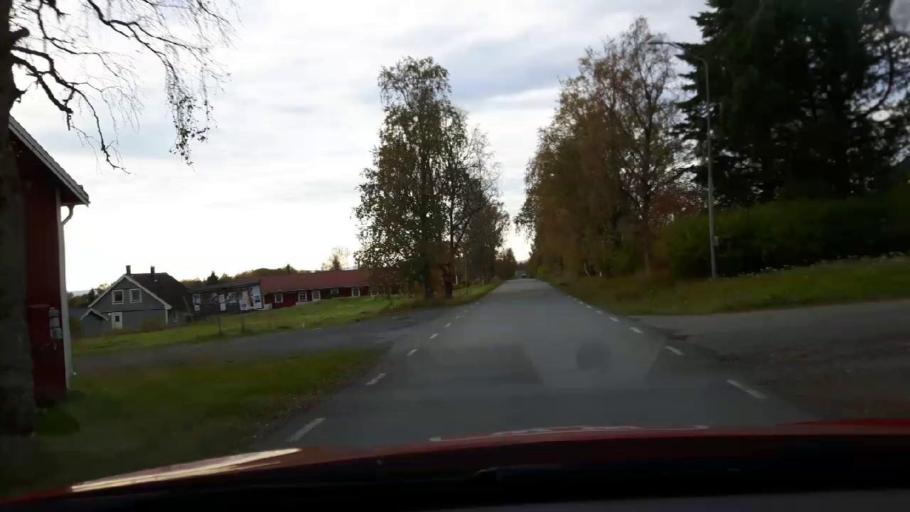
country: SE
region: Jaemtland
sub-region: Krokoms Kommun
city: Krokom
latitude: 63.3674
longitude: 14.4831
